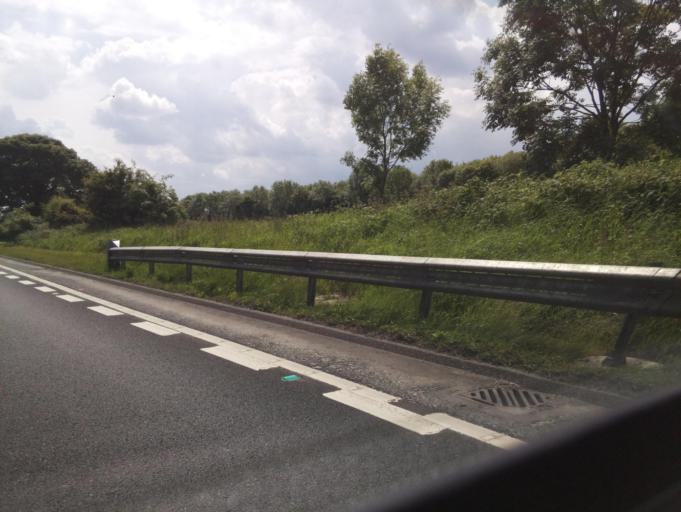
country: GB
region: England
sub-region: Stockton-on-Tees
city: Yarm
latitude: 54.3897
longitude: -1.3192
